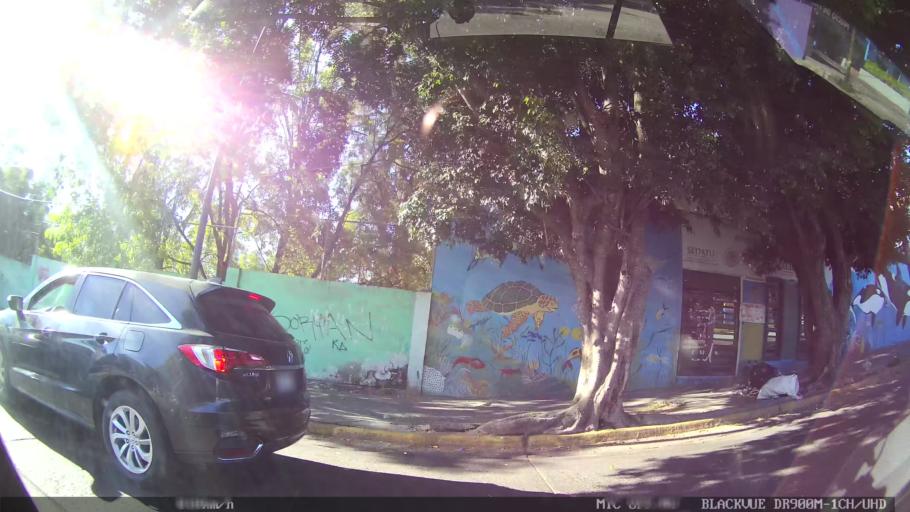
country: MX
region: Jalisco
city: Tlaquepaque
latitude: 20.6999
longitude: -103.2900
